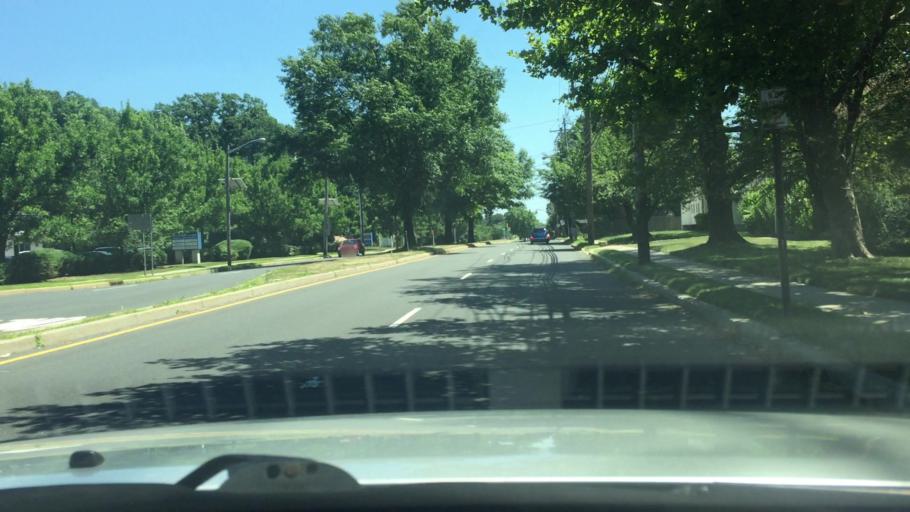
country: US
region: New Jersey
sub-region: Middlesex County
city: South River
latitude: 40.4273
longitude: -74.3911
